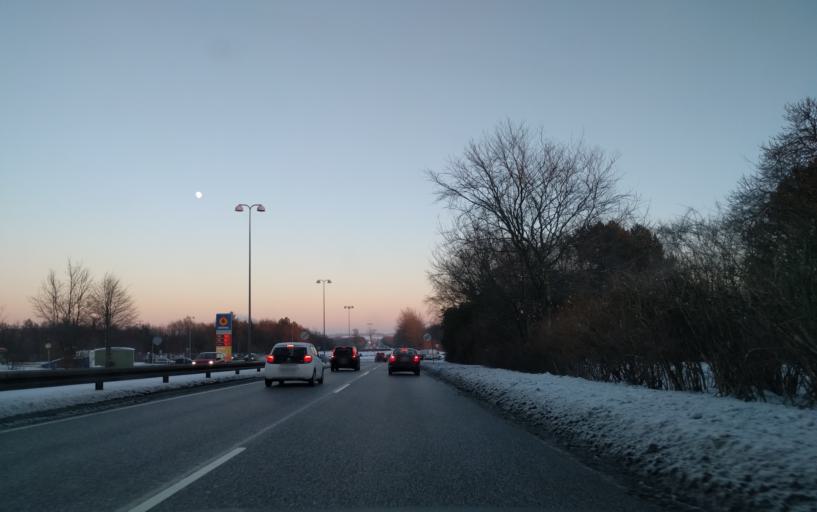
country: DK
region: North Denmark
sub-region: Alborg Kommune
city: Gistrup
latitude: 57.0200
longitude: 9.9663
